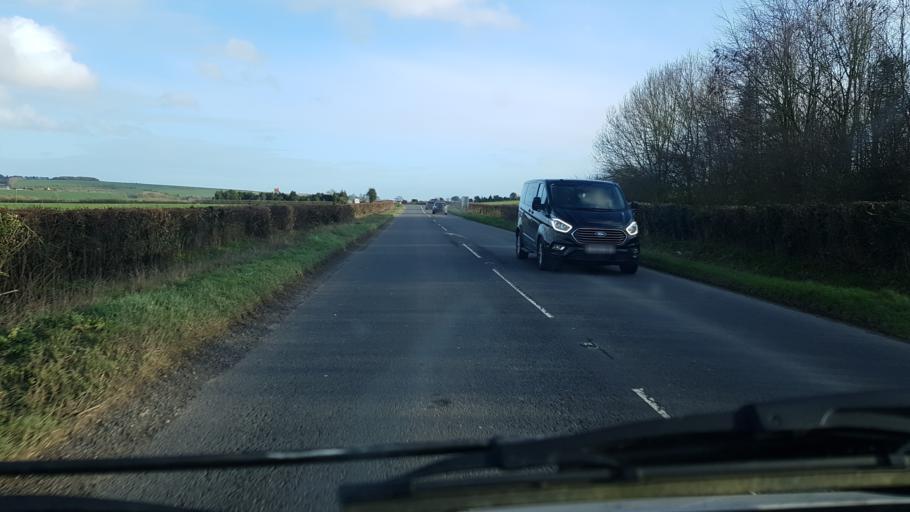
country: GB
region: England
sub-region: Wiltshire
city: Collingbourne Kingston
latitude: 51.3214
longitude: -1.6727
